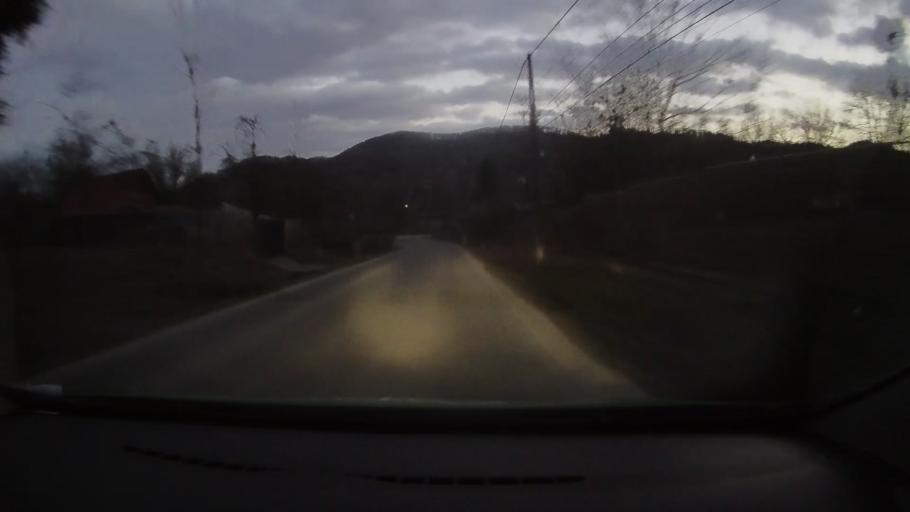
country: RO
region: Prahova
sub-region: Comuna Provita de Jos
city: Provita de Jos
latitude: 45.1216
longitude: 25.6620
